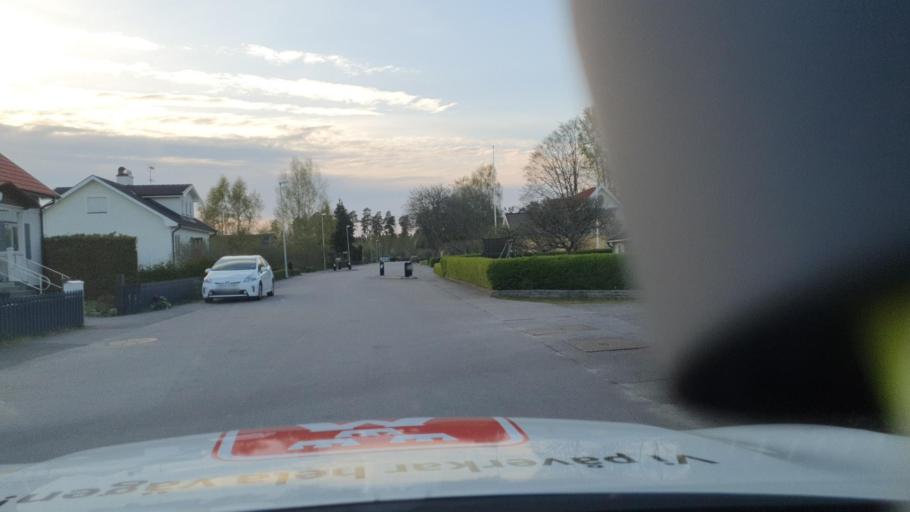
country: SE
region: OEstergoetland
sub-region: Linkopings Kommun
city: Vikingstad
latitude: 58.3840
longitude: 15.4268
